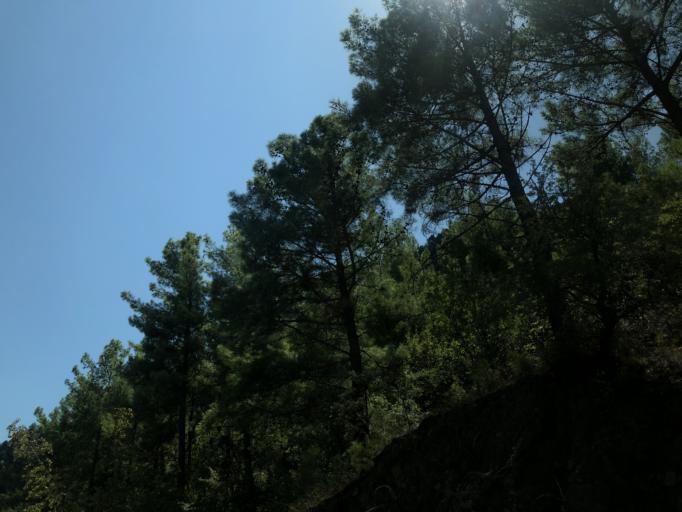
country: TR
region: Antalya
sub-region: Manavgat
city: Manavgat
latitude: 36.9100
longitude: 31.5508
